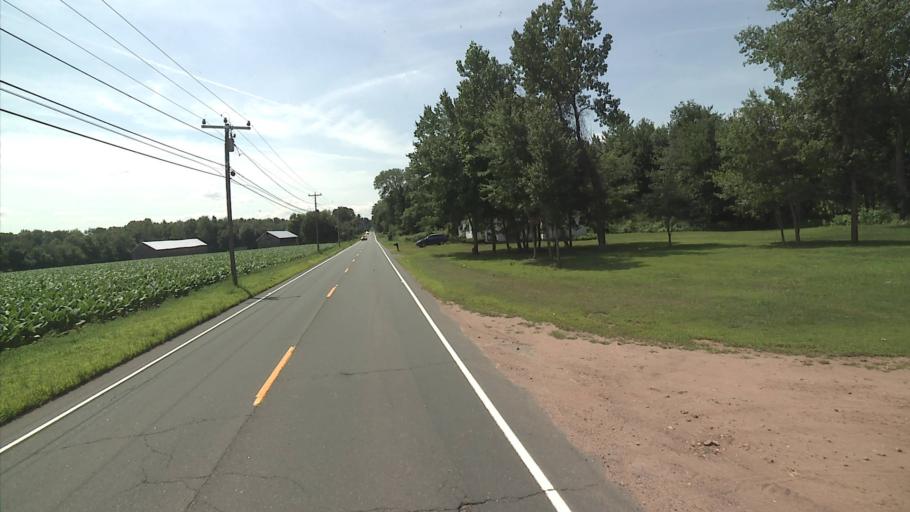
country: US
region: Connecticut
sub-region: Tolland County
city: Ellington
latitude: 41.8902
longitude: -72.4811
